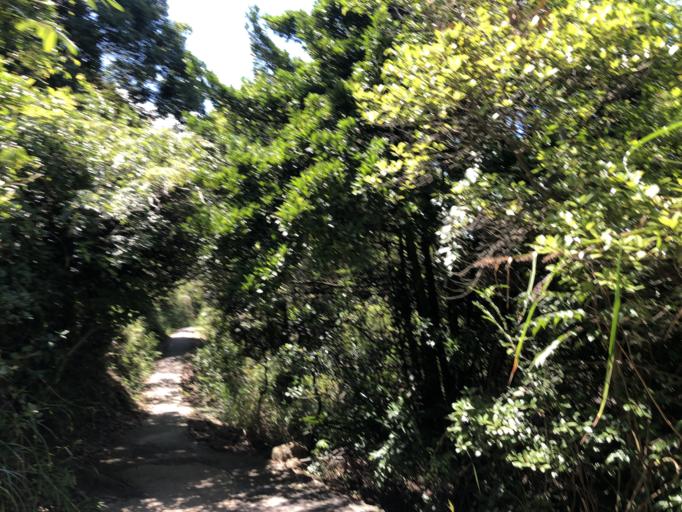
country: HK
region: Tuen Mun
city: Tuen Mun
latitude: 22.2843
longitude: 113.9823
